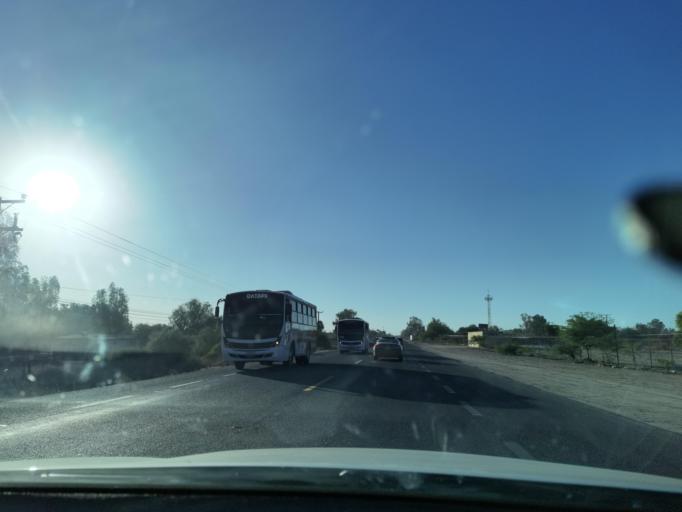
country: MX
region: Baja California
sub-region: Mexicali
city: Islas Agrarias Grupo A
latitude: 32.6452
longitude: -115.3191
